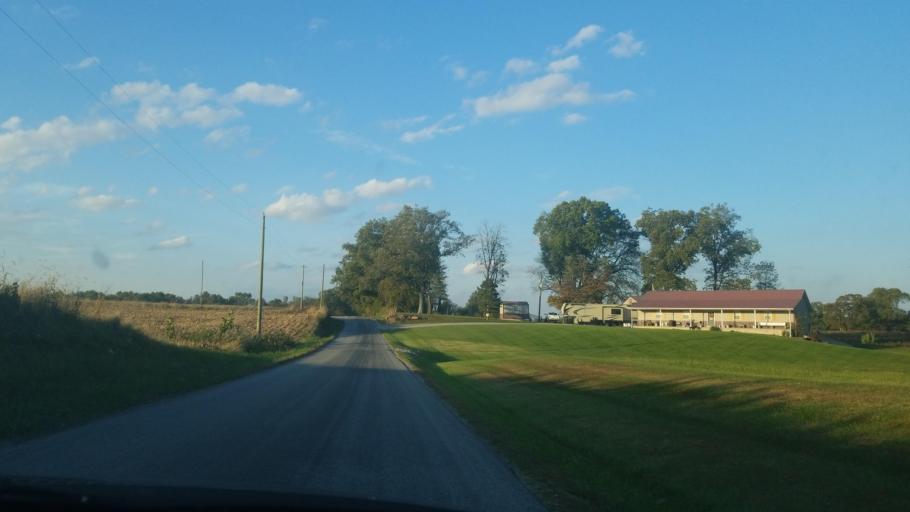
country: US
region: Illinois
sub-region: Saline County
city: Harrisburg
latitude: 37.8109
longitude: -88.6146
